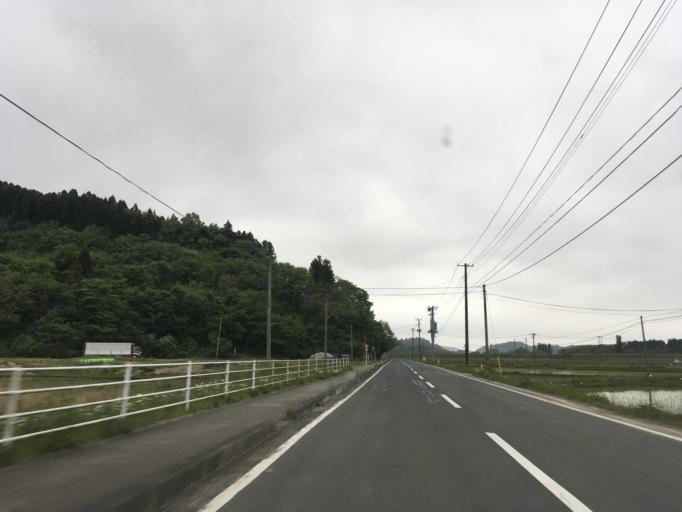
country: JP
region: Miyagi
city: Wakuya
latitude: 38.7250
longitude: 141.2964
